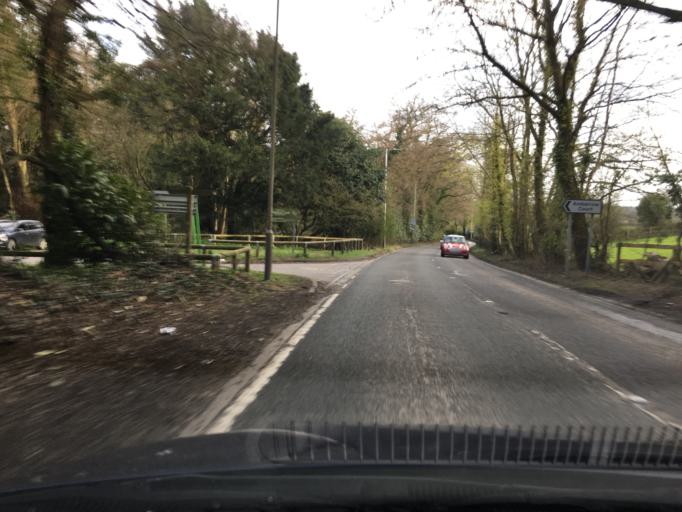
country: GB
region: England
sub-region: Hampshire
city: Yateley
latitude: 51.3575
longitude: -0.8174
